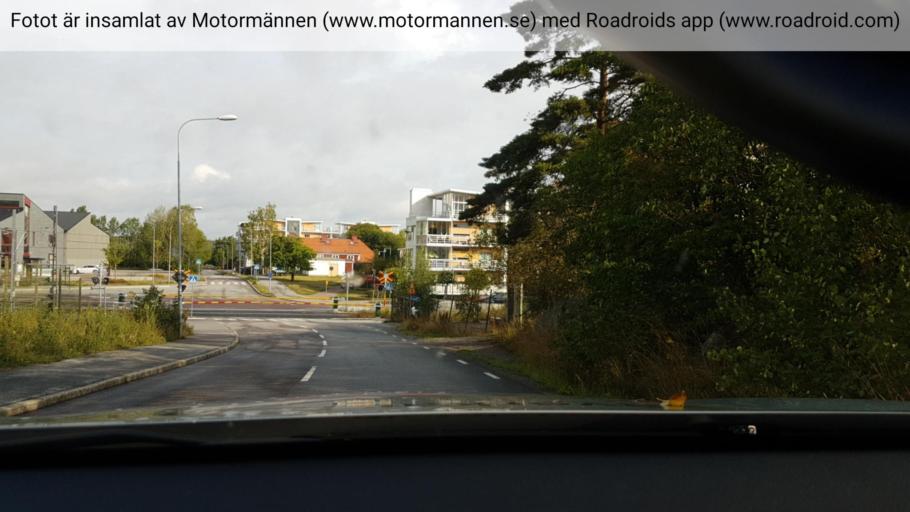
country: SE
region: Stockholm
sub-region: Lidingo
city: Brevik
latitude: 59.3561
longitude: 18.2304
